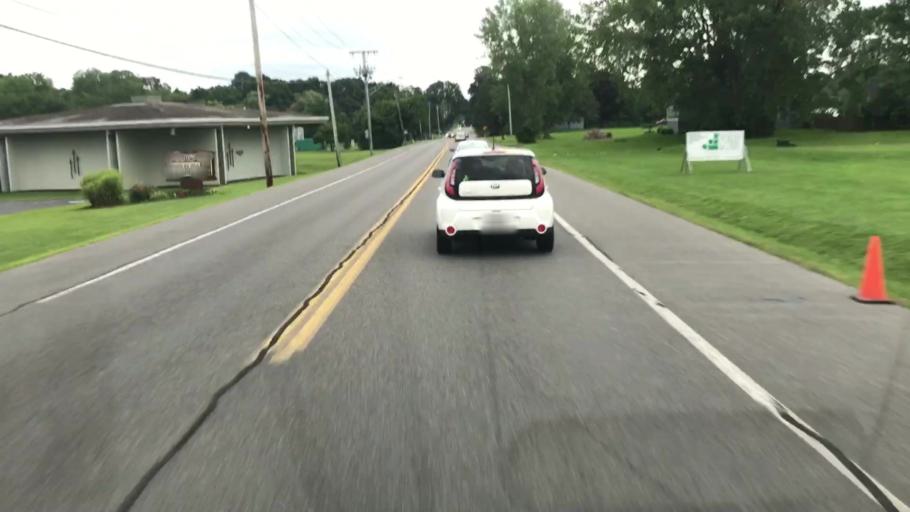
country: US
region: New York
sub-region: Onondaga County
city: North Syracuse
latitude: 43.1327
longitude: -76.1654
